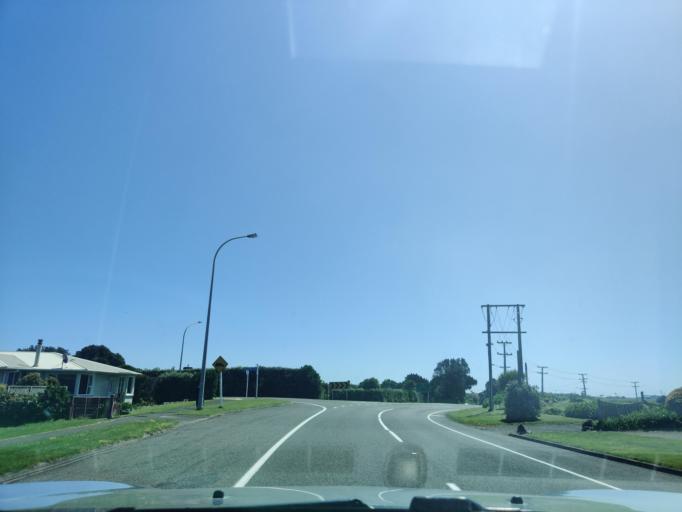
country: NZ
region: Taranaki
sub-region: South Taranaki District
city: Opunake
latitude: -39.4492
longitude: 173.8469
